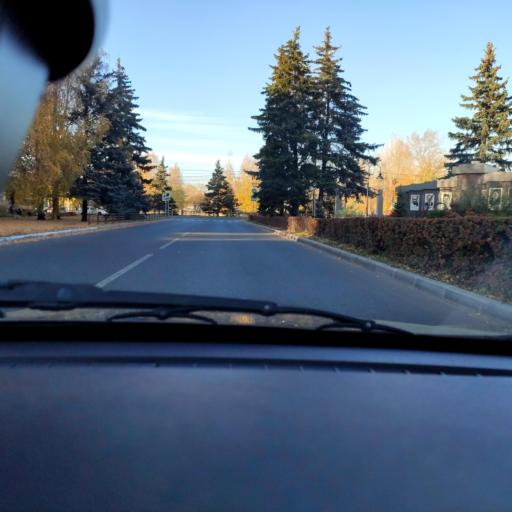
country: RU
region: Samara
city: Tol'yatti
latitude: 53.5078
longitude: 49.4185
